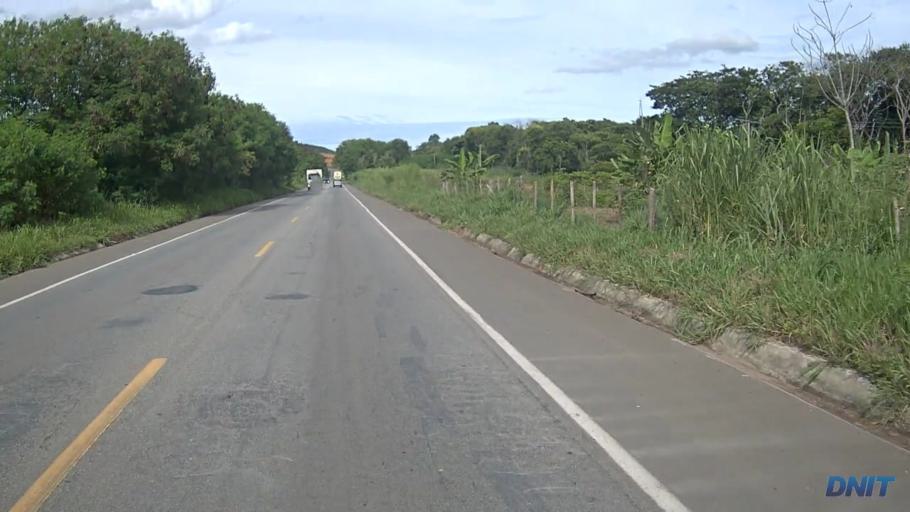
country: BR
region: Minas Gerais
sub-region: Ipaba
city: Ipaba
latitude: -19.2970
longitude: -42.3658
